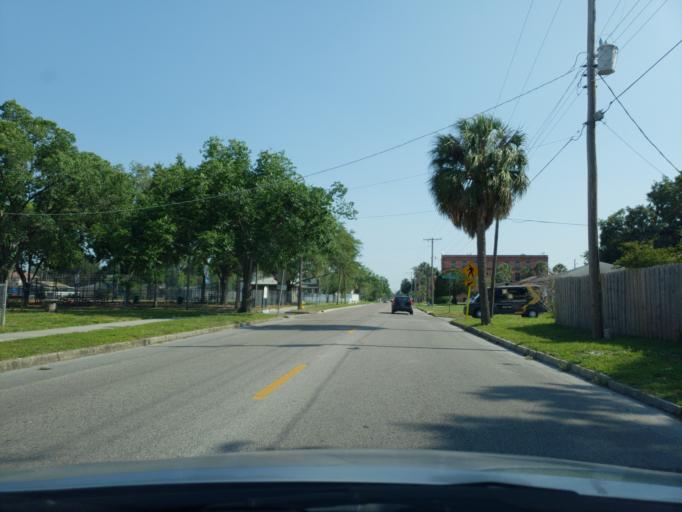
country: US
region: Florida
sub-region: Hillsborough County
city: Tampa
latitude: 27.9692
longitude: -82.4890
